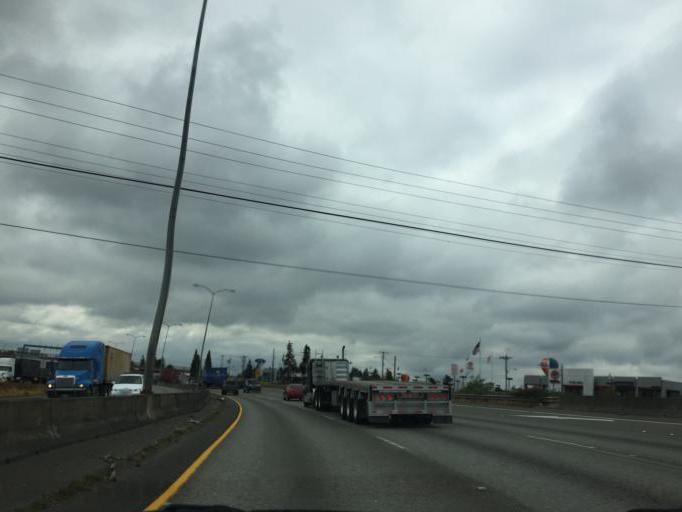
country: US
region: Washington
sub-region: Pierce County
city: Tacoma
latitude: 47.2286
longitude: -122.4630
